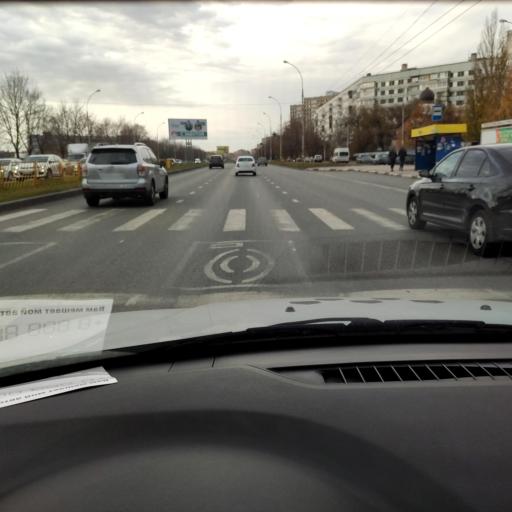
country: RU
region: Samara
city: Tol'yatti
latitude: 53.5284
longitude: 49.3346
